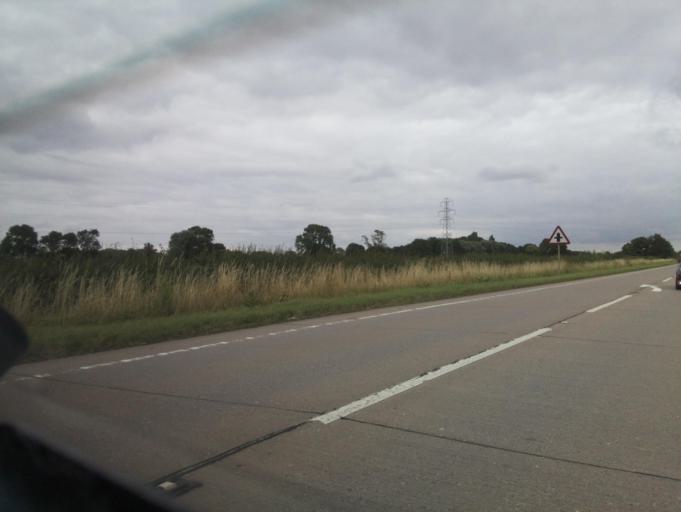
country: GB
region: England
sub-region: Lincolnshire
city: Long Bennington
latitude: 52.9344
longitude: -0.8147
